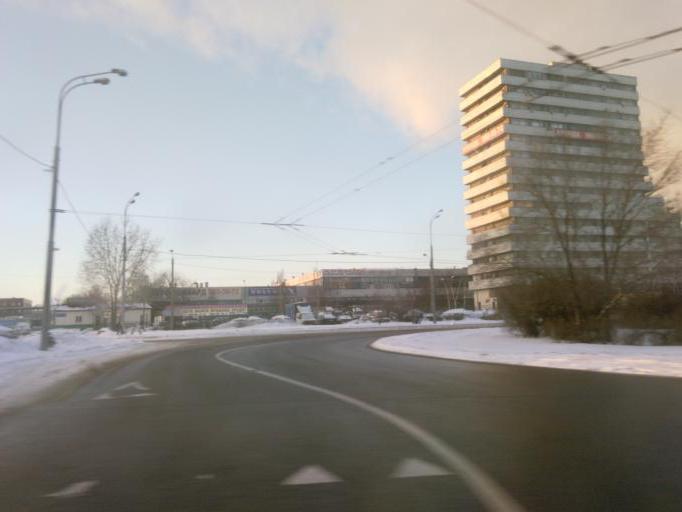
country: RU
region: Moskovskaya
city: Vostryakovo
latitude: 55.6693
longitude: 37.4461
